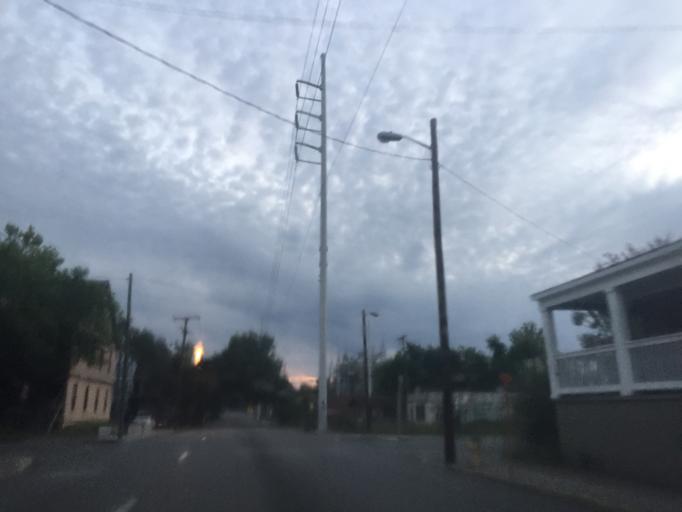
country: US
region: Georgia
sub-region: Chatham County
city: Savannah
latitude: 32.0628
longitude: -81.0901
